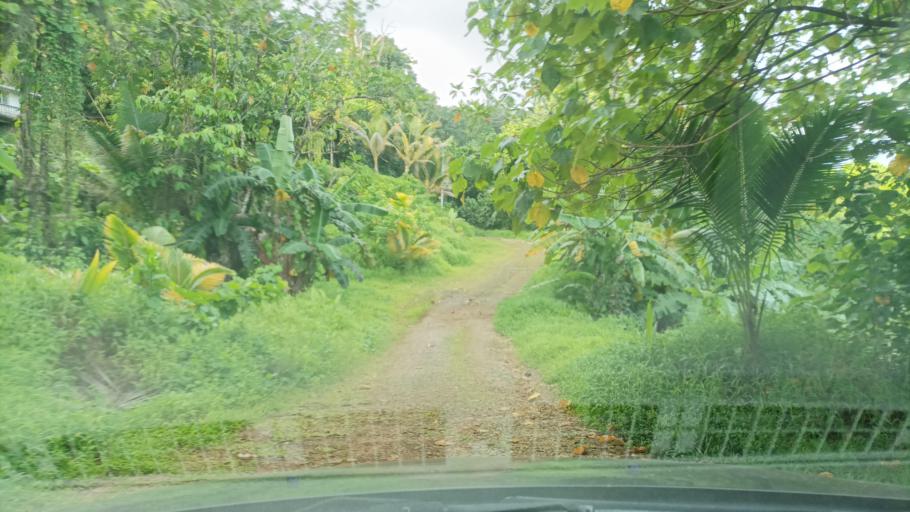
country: FM
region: Kosrae
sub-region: Utwe Municipality
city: Utwe
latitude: 5.2747
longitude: 162.9500
